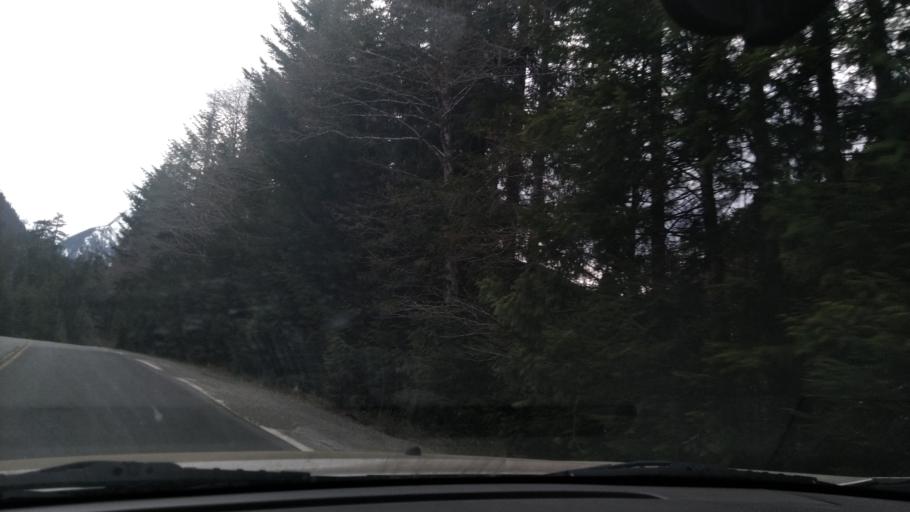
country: CA
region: British Columbia
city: Campbell River
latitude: 49.8434
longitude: -125.8604
